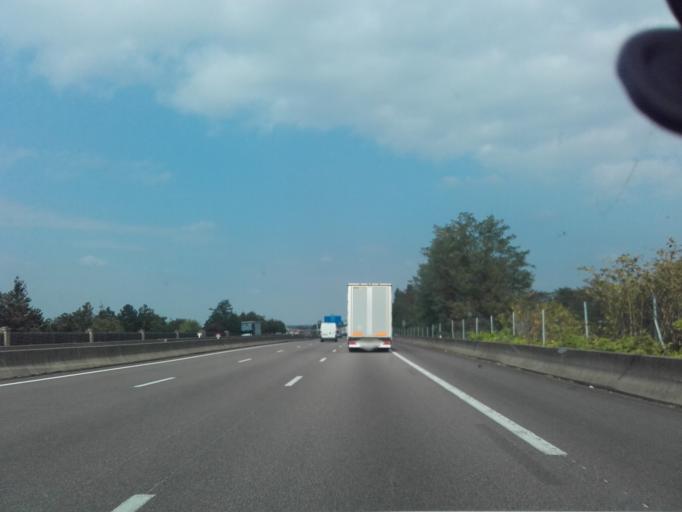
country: FR
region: Bourgogne
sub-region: Departement de Saone-et-Loire
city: Chatenoy-le-Royal
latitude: 46.7974
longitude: 4.8237
